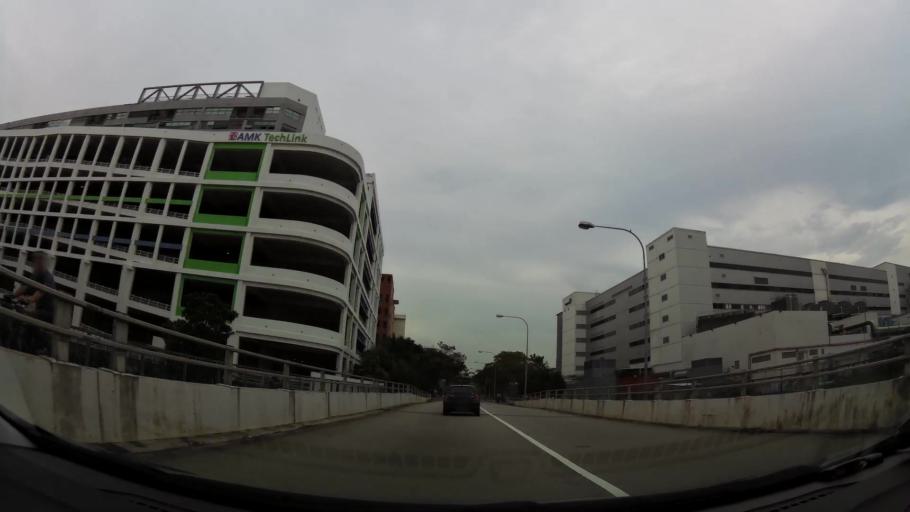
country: SG
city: Singapore
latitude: 1.3765
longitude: 103.8716
